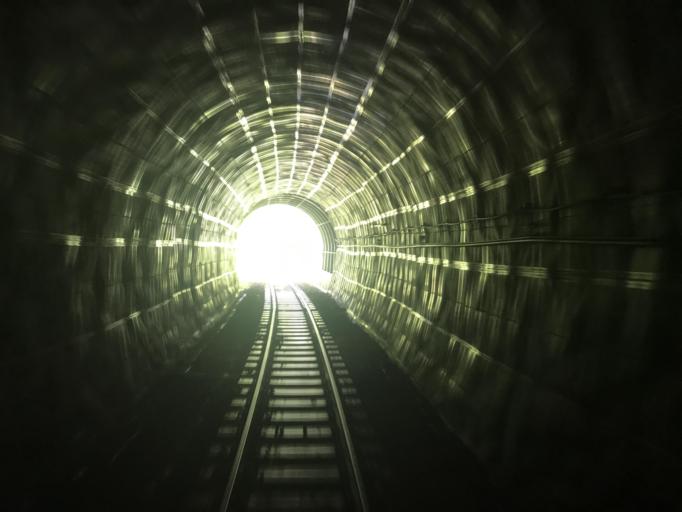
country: JP
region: Yamagata
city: Nagai
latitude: 38.0196
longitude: 139.9098
